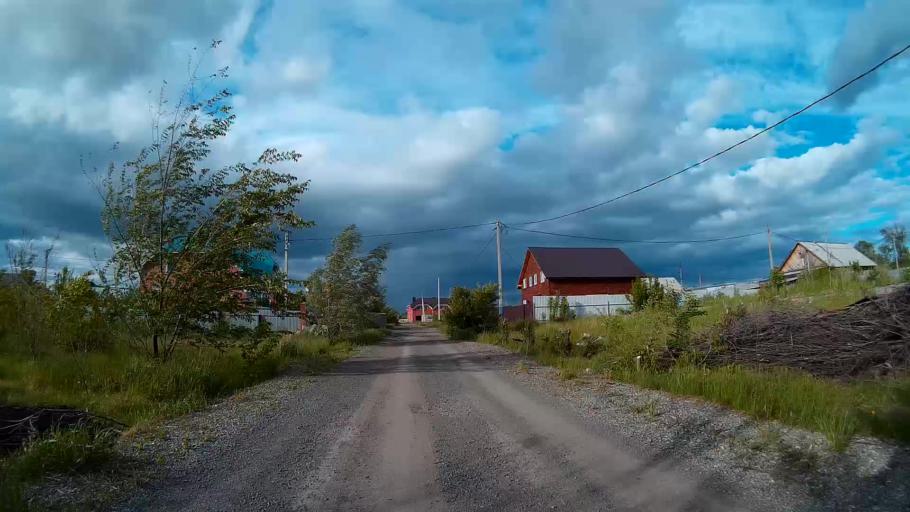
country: RU
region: Ulyanovsk
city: Novoul'yanovsk
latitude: 54.2001
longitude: 48.2730
